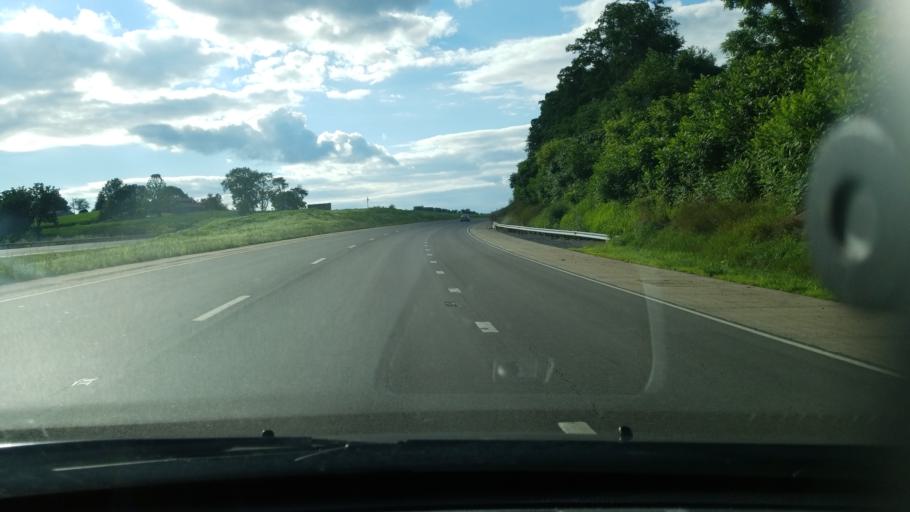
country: US
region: Pennsylvania
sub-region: Northumberland County
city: Milton
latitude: 41.0241
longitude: -76.7991
